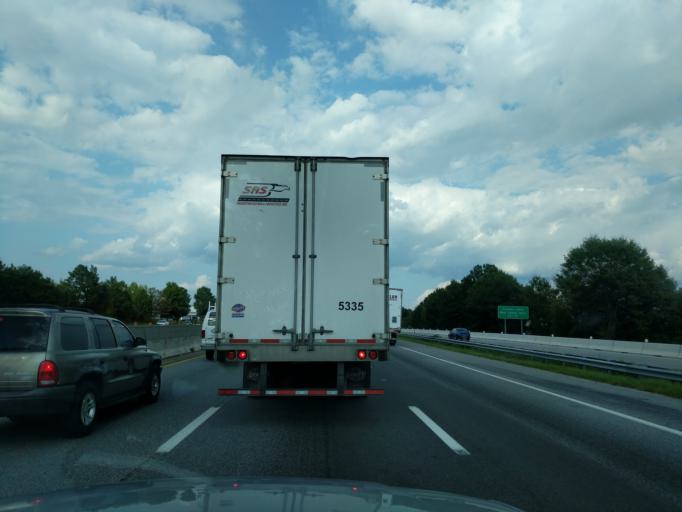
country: US
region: South Carolina
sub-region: Greenville County
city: Mauldin
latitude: 34.8266
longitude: -82.3073
